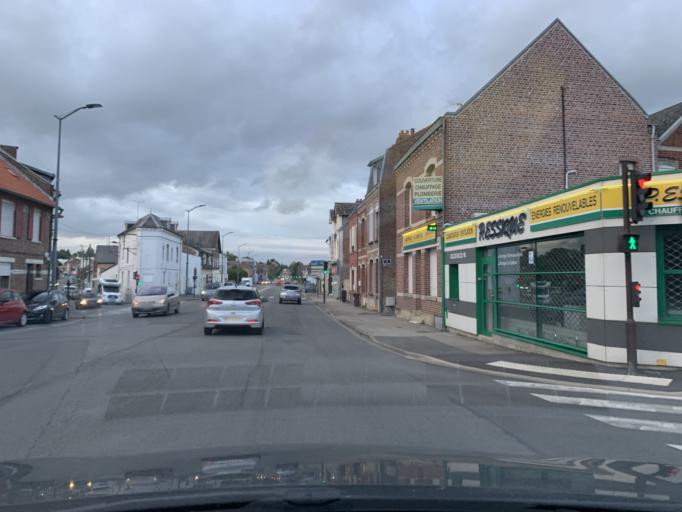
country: FR
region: Picardie
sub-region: Departement de l'Aisne
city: Saint-Quentin
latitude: 49.8561
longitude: 3.2791
